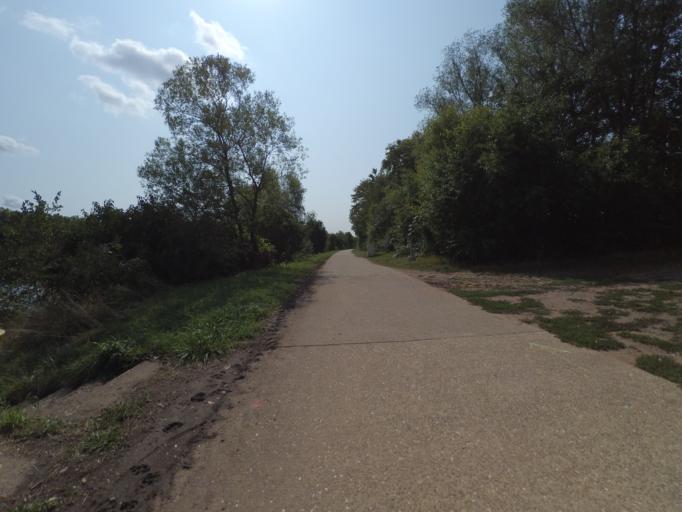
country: DE
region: Saarland
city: Merzig
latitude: 49.4485
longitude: 6.6309
